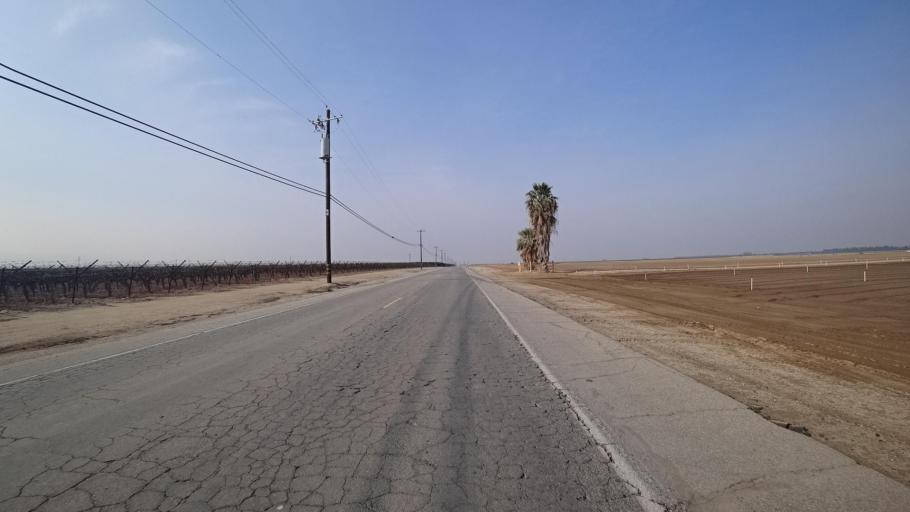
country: US
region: California
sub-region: Kern County
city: Weedpatch
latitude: 35.0931
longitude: -118.9404
